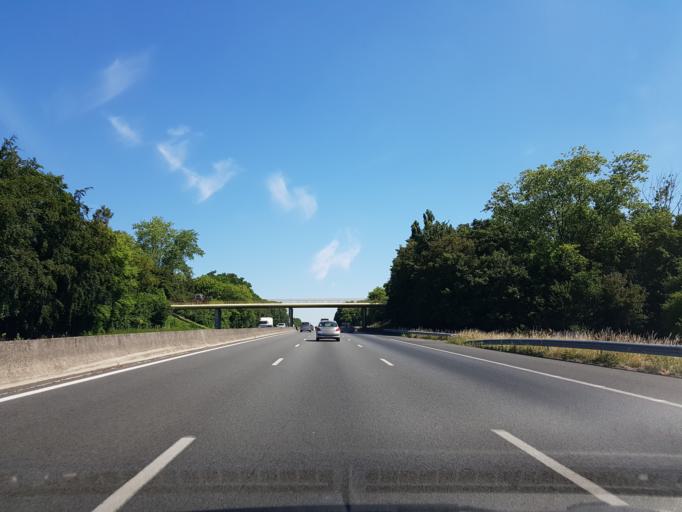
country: FR
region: Picardie
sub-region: Departement de l'Oise
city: Ressons-sur-Matz
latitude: 49.5561
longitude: 2.7335
